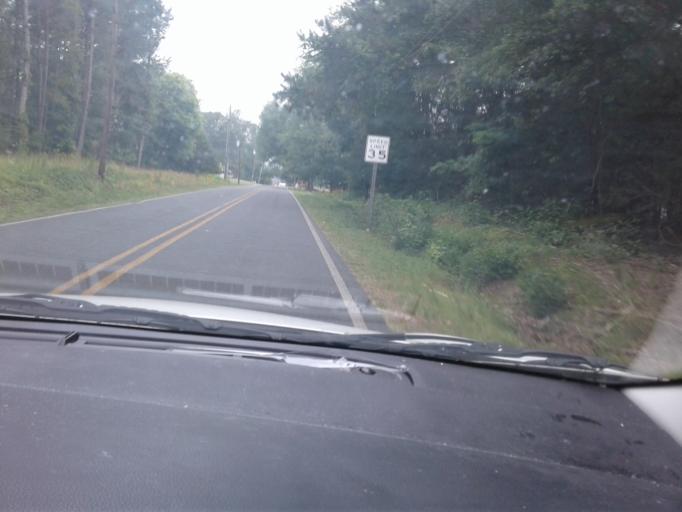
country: US
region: North Carolina
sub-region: Harnett County
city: Buies Creek
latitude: 35.4121
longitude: -78.7301
